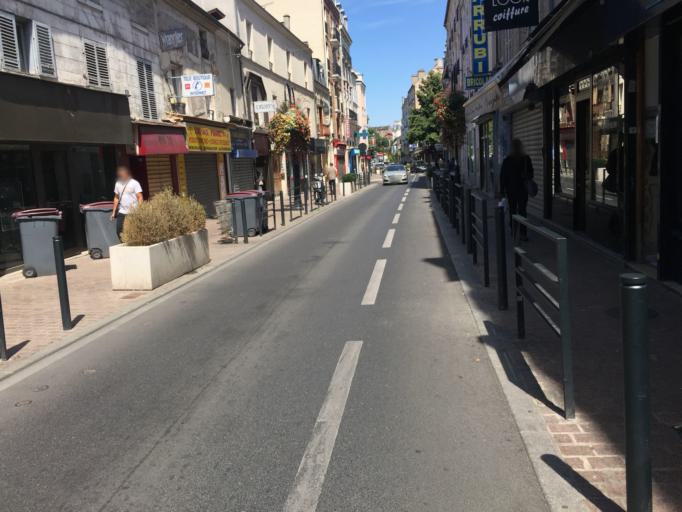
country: FR
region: Ile-de-France
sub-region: Departement du Val-d'Oise
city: Argenteuil
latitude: 48.9451
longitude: 2.2524
